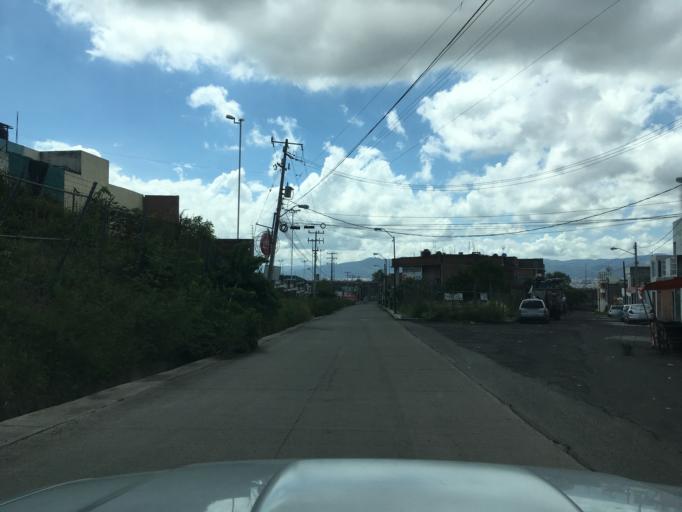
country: MX
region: Michoacan
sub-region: Tarimbaro
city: Fraccionamiento Metropolis II
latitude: 19.7253
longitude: -101.2272
